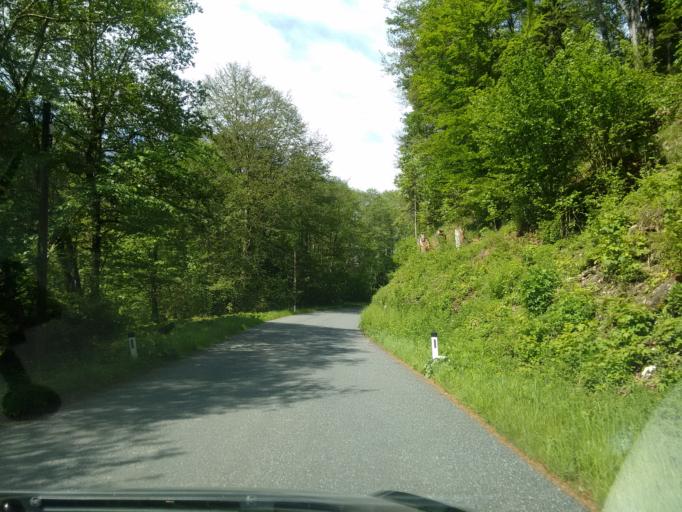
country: AT
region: Upper Austria
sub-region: Politischer Bezirk Gmunden
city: Ebensee
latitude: 47.8391
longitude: 13.7139
